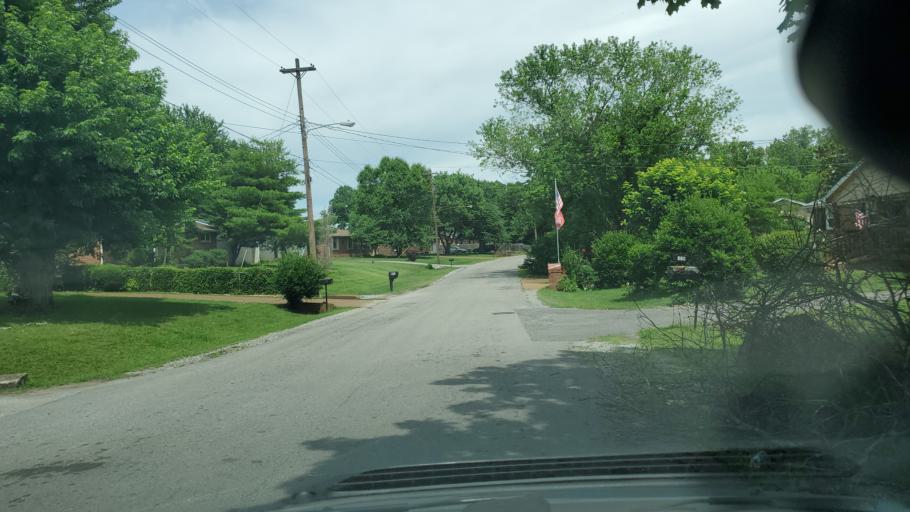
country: US
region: Tennessee
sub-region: Davidson County
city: Oak Hill
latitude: 36.1167
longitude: -86.7014
